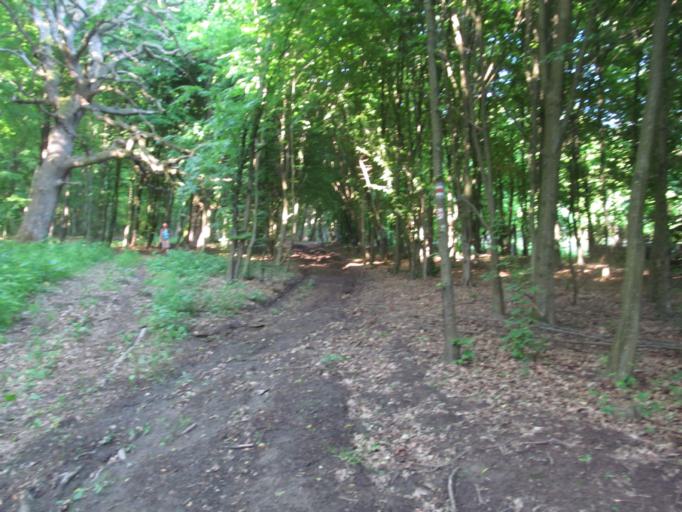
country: HU
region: Borsod-Abauj-Zemplen
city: Gonc
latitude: 48.5260
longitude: 21.4384
